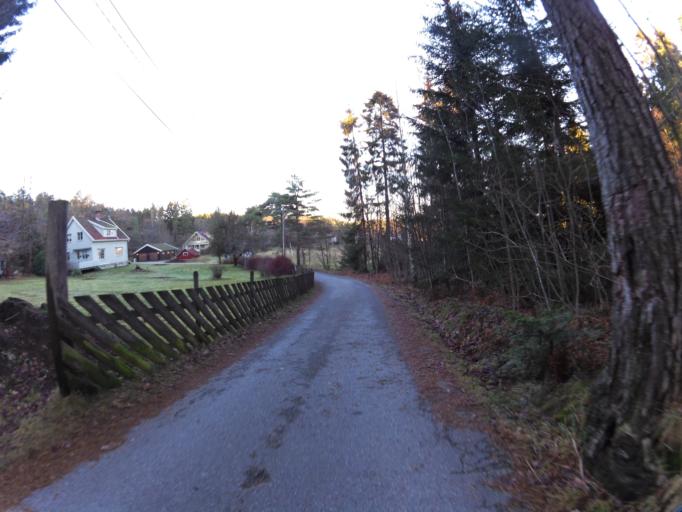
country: NO
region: Ostfold
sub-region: Fredrikstad
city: Fredrikstad
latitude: 59.2419
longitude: 10.9644
